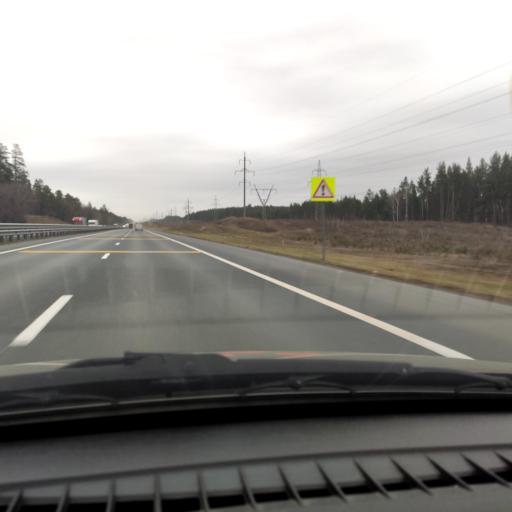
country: RU
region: Samara
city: Povolzhskiy
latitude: 53.5163
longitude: 49.7151
